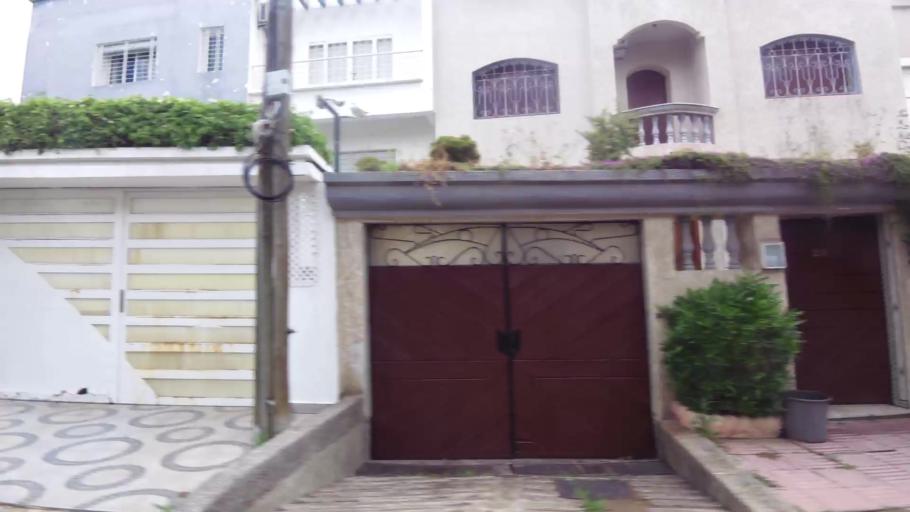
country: MA
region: Grand Casablanca
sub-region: Nouaceur
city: Bouskoura
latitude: 33.5186
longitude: -7.6463
